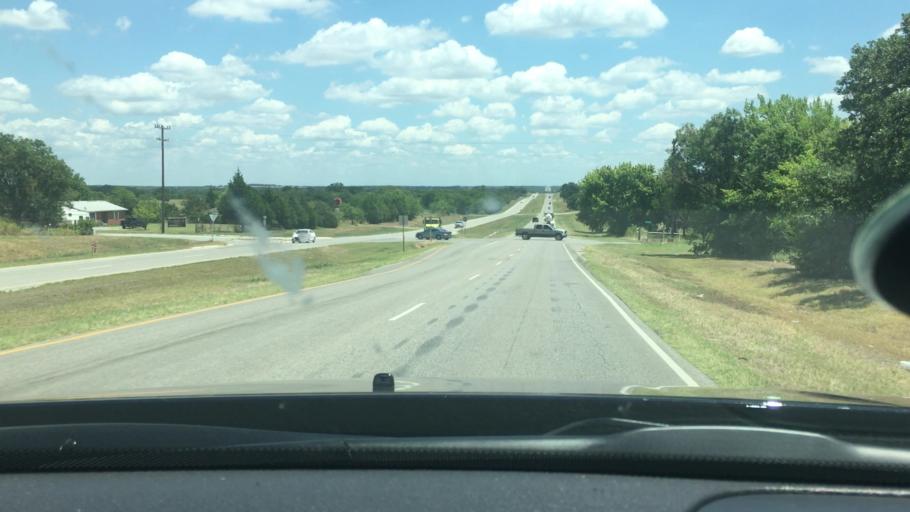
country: US
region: Oklahoma
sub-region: Carter County
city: Wilson
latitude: 34.1728
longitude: -97.4057
